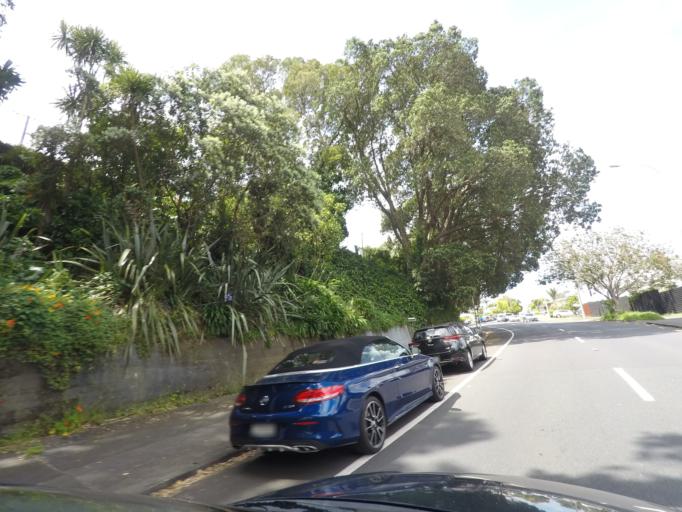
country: NZ
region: Auckland
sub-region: Auckland
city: Auckland
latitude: -36.8502
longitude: 174.7276
